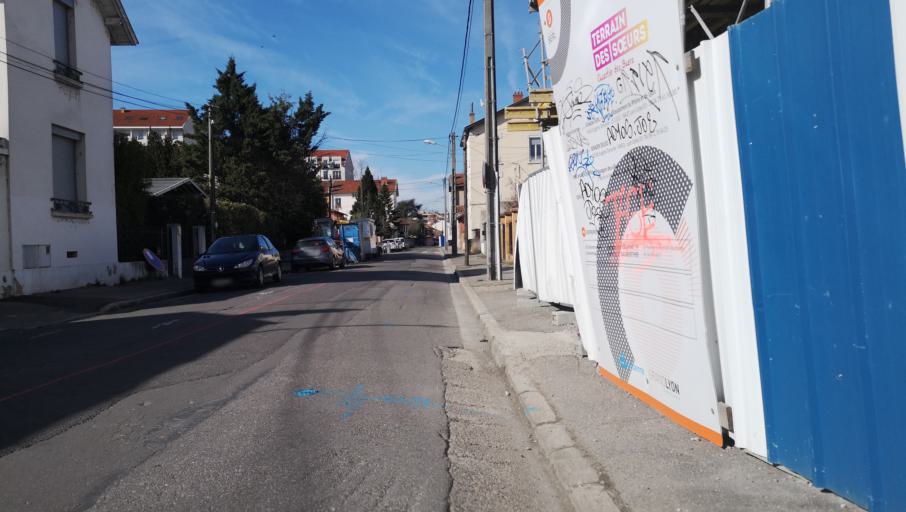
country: FR
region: Rhone-Alpes
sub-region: Departement du Rhone
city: Villeurbanne
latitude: 45.7803
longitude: 4.8882
